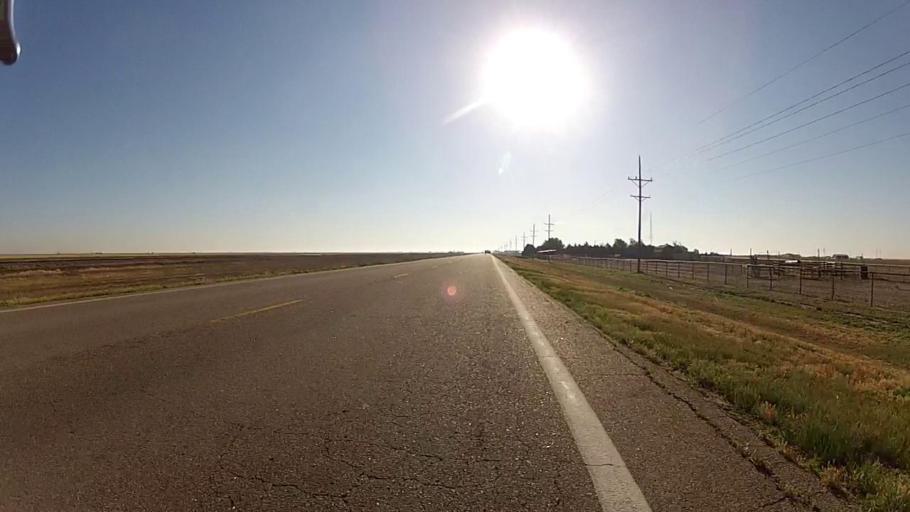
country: US
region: Kansas
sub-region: Haskell County
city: Sublette
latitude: 37.4925
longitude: -100.8111
